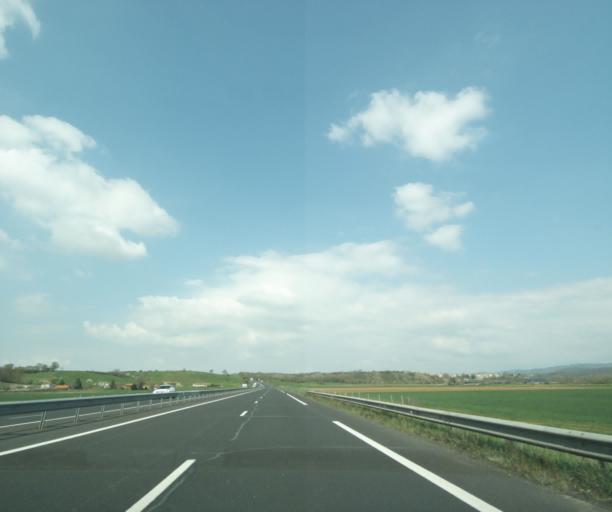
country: FR
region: Auvergne
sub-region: Departement de la Haute-Loire
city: Lempdes-sur-Allagnon
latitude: 45.4027
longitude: 3.2737
